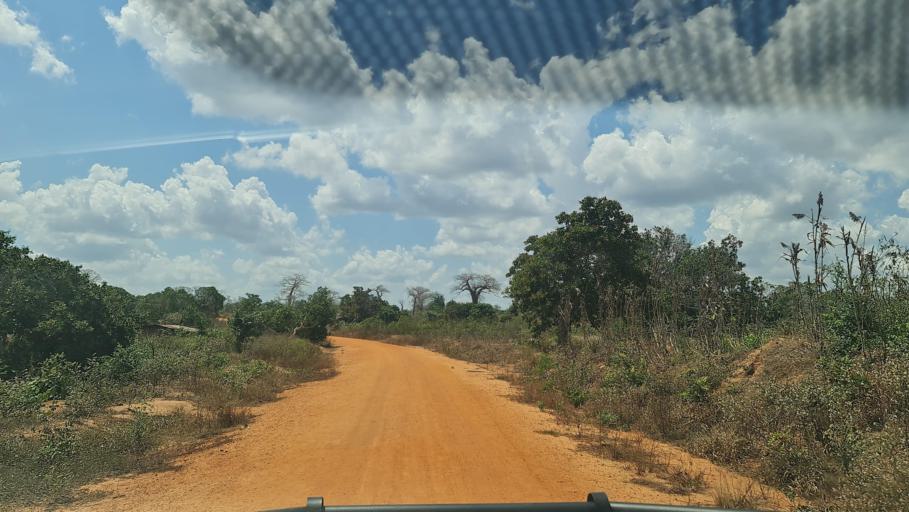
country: MZ
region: Nampula
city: Ilha de Mocambique
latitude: -15.0544
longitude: 40.2394
